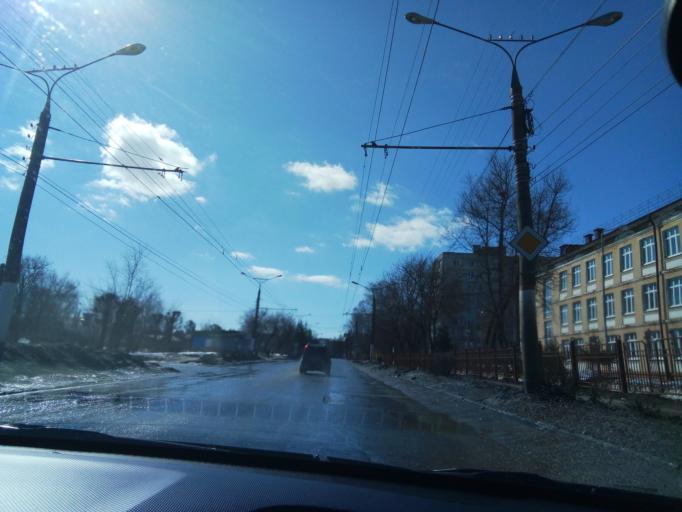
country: RU
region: Chuvashia
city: Novyye Lapsary
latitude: 56.1106
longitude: 47.1815
